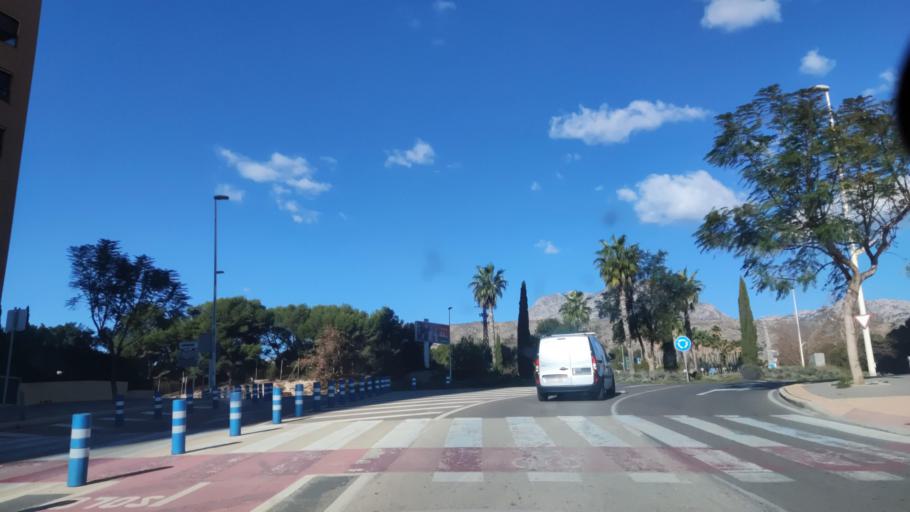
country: ES
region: Valencia
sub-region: Provincia de Alicante
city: Benidorm
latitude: 38.5371
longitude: -0.1580
